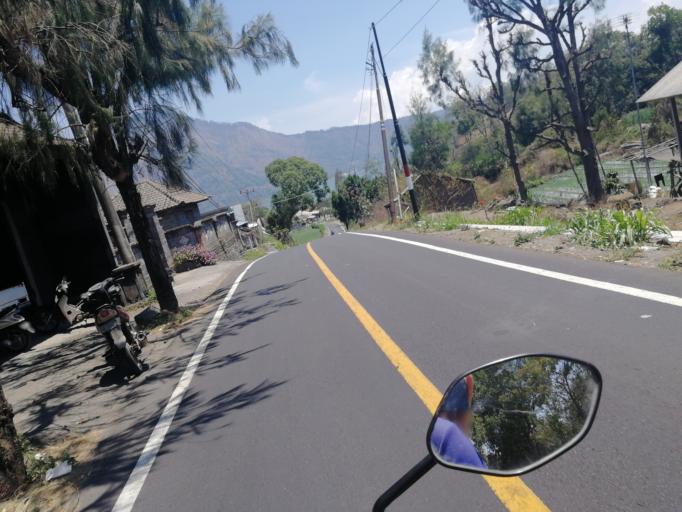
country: ID
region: Bali
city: Banjar Trunyan
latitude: -8.2345
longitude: 115.4055
